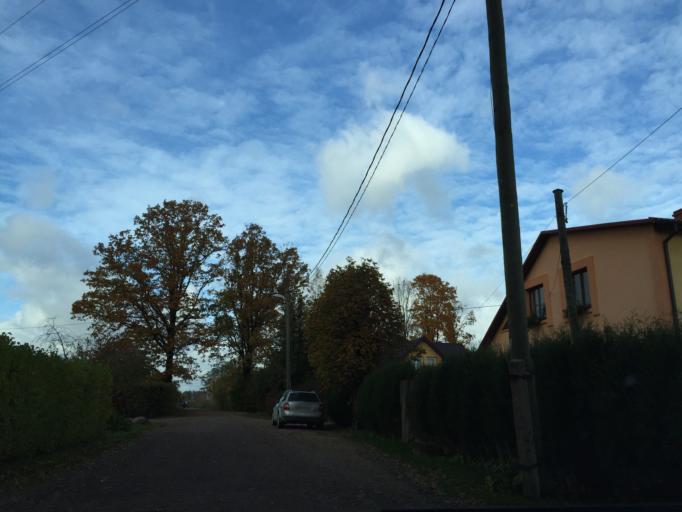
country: LV
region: Lielvarde
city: Lielvarde
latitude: 56.7180
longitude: 24.8319
